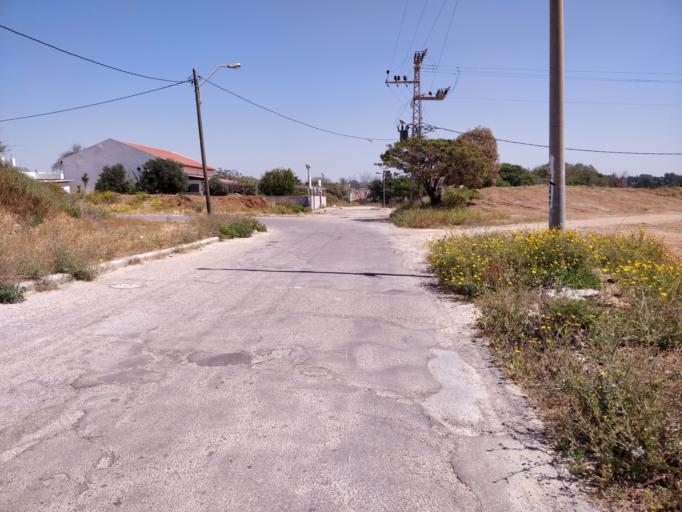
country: IL
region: Central District
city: Netanya
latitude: 32.3504
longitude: 34.8570
